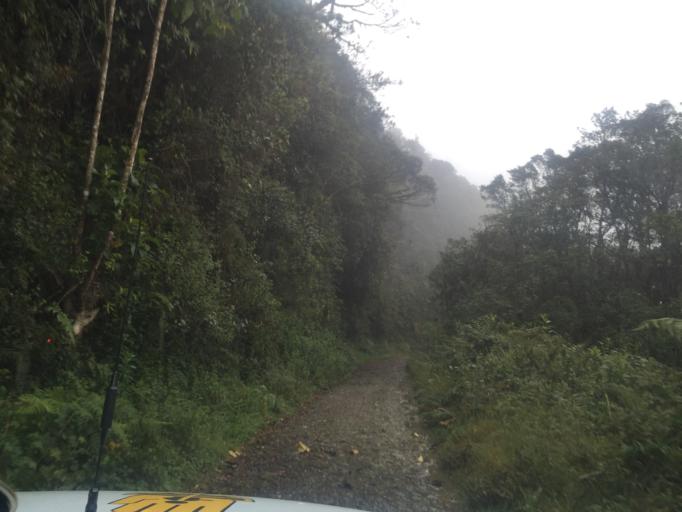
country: CO
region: Quindio
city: Calarca
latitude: 4.4754
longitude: -75.5628
